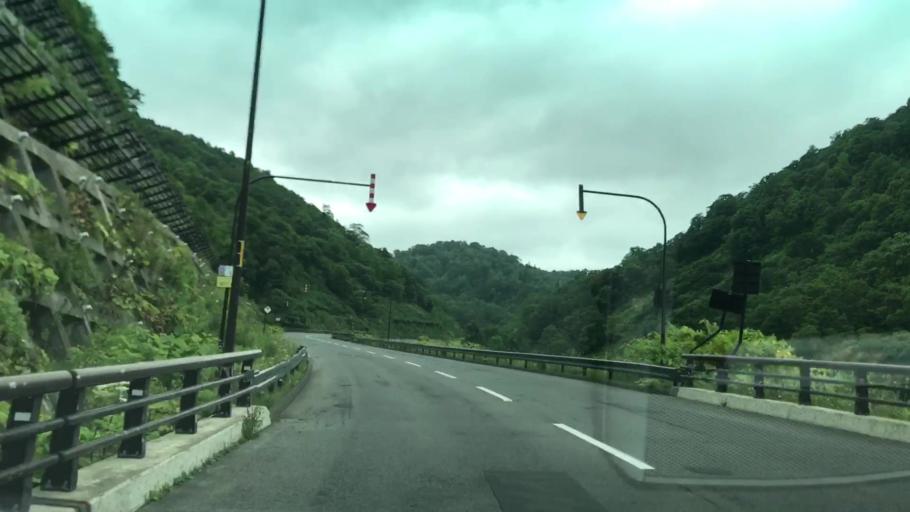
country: JP
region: Hokkaido
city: Yoichi
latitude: 42.9867
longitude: 140.8721
